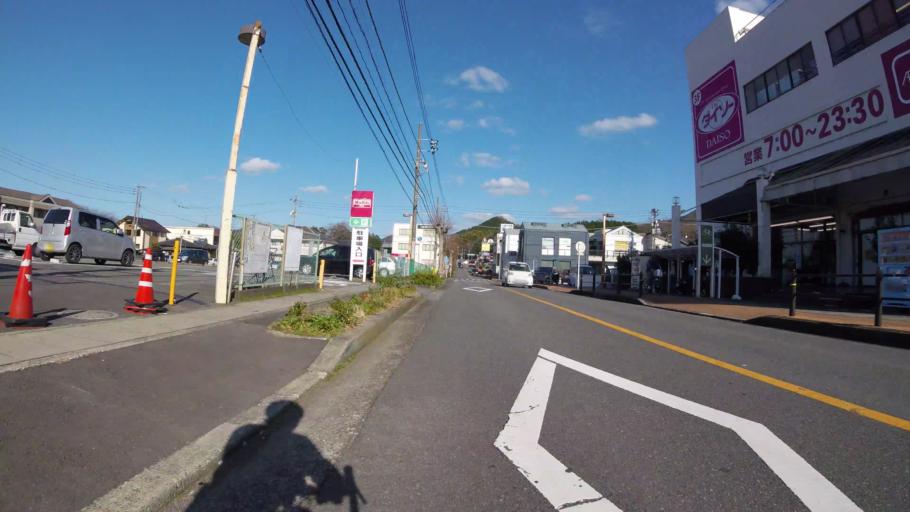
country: JP
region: Shizuoka
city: Ito
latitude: 34.9813
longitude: 138.9519
